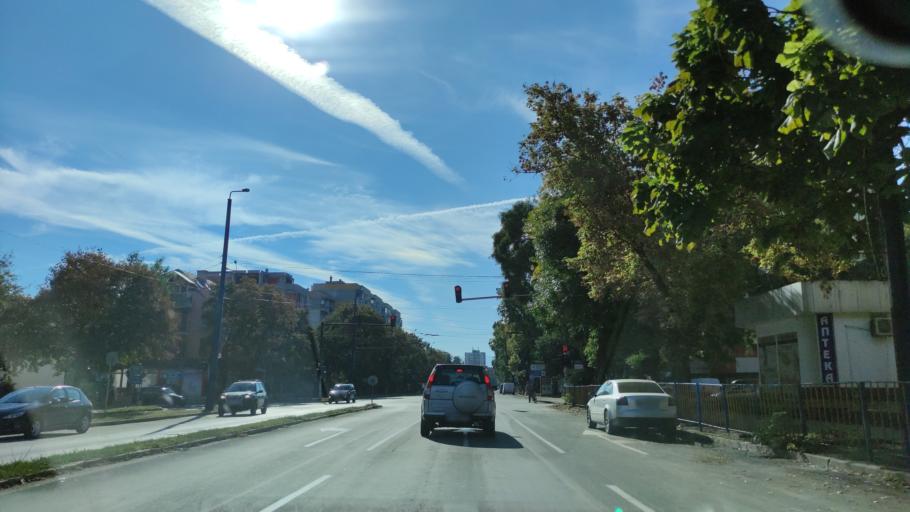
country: BG
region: Pazardzhik
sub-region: Obshtina Pazardzhik
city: Pazardzhik
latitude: 42.2056
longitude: 24.3294
